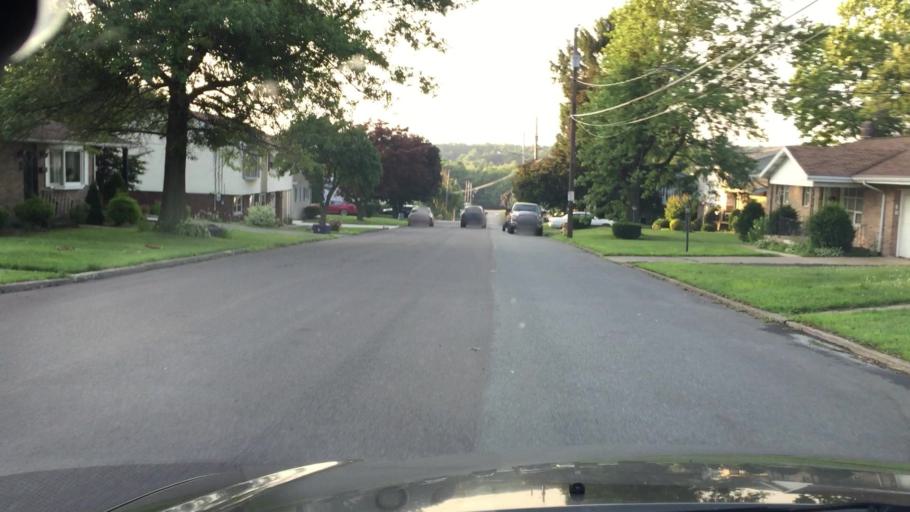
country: US
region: Pennsylvania
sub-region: Luzerne County
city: Harleigh
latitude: 40.9724
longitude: -75.9726
